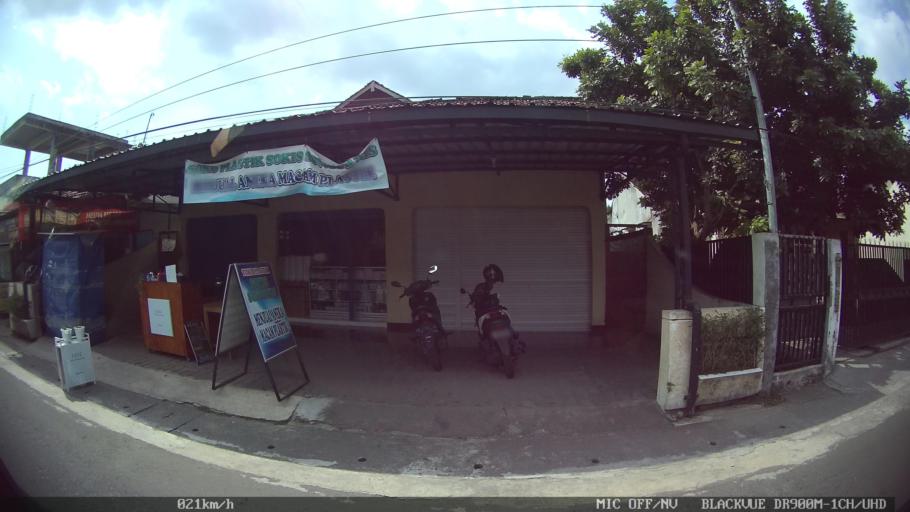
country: ID
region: Daerah Istimewa Yogyakarta
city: Gamping Lor
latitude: -7.8061
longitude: 110.3379
